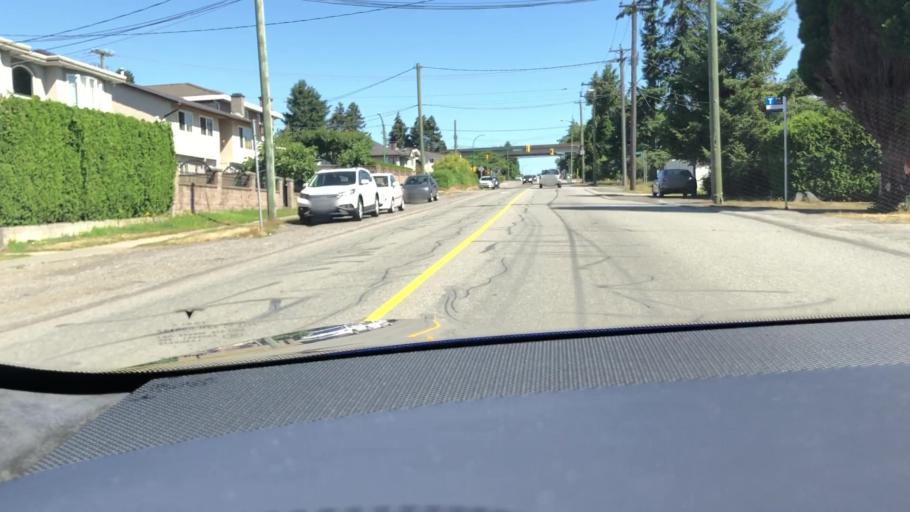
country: CA
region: British Columbia
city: Burnaby
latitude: 49.2132
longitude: -122.9719
